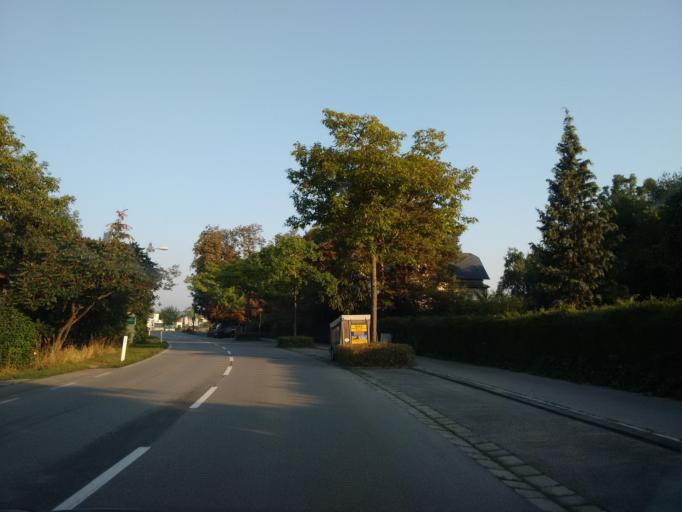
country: AT
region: Upper Austria
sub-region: Wels Stadt
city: Wels
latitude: 48.1756
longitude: 14.0161
